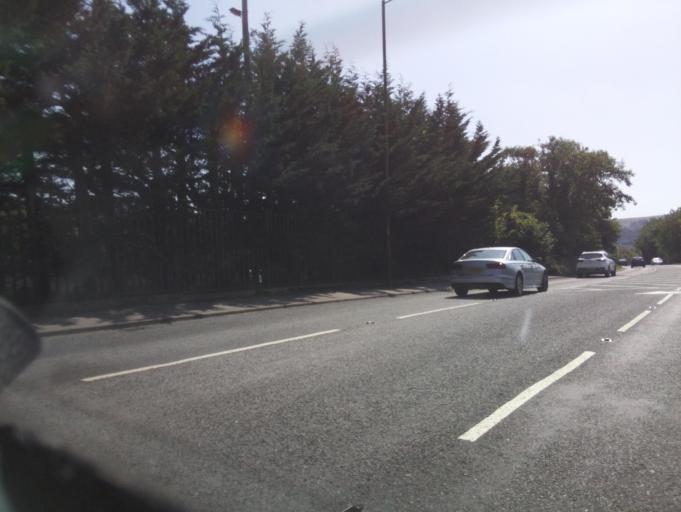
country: GB
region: Wales
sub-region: Caerphilly County Borough
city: Hengoed
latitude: 51.6458
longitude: -3.2251
